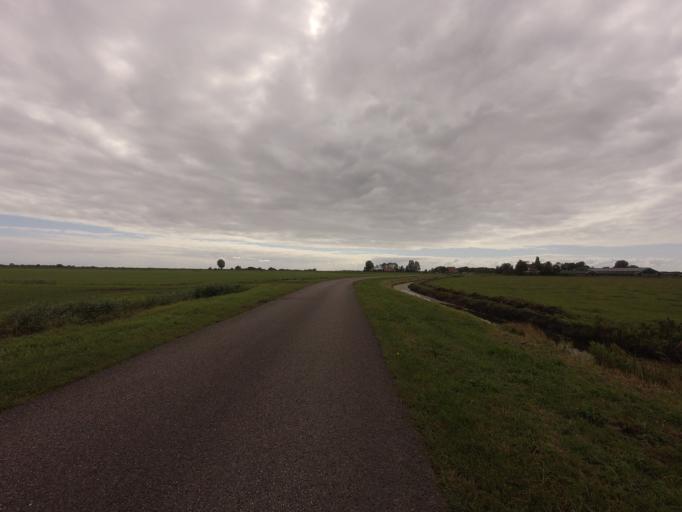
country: NL
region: Friesland
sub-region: Gemeente Gaasterlan-Sleat
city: Balk
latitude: 52.9533
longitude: 5.5296
